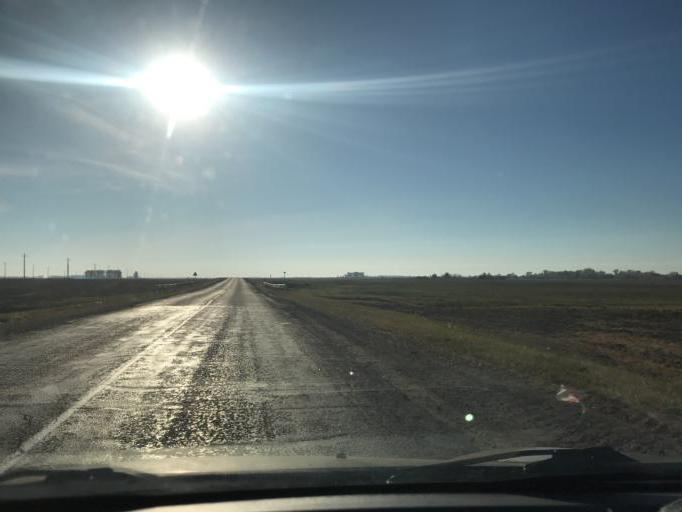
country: BY
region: Gomel
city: Khoyniki
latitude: 51.8441
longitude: 30.0317
